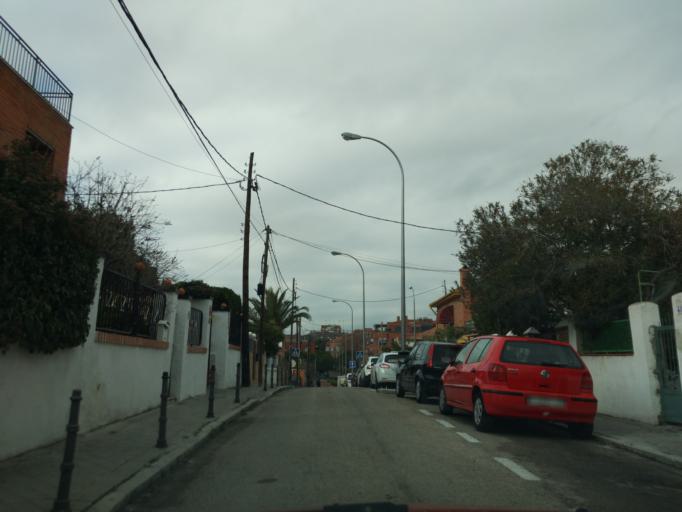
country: ES
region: Madrid
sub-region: Provincia de Madrid
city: Ciudad Lineal
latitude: 40.4658
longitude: -3.6501
